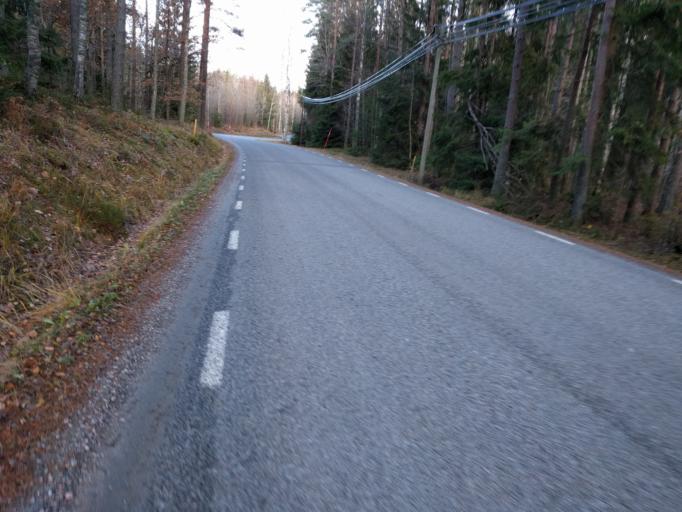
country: SE
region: Stockholm
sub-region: Osterakers Kommun
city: Akersberga
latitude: 59.5978
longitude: 18.3526
